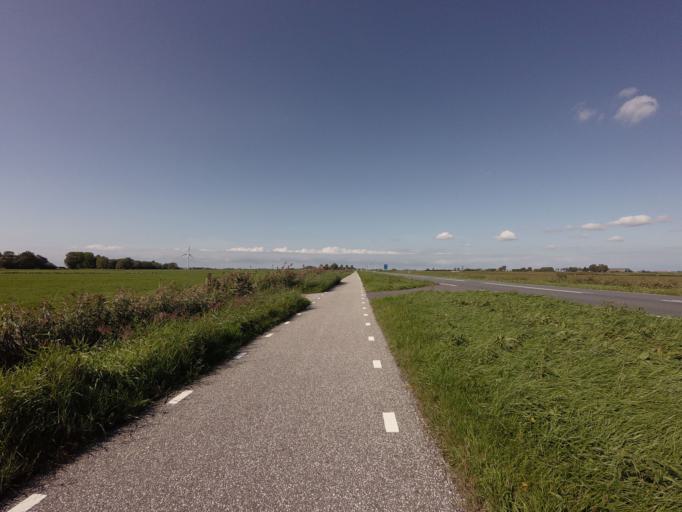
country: NL
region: Friesland
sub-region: Gemeente Littenseradiel
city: Makkum
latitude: 53.1121
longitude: 5.6849
